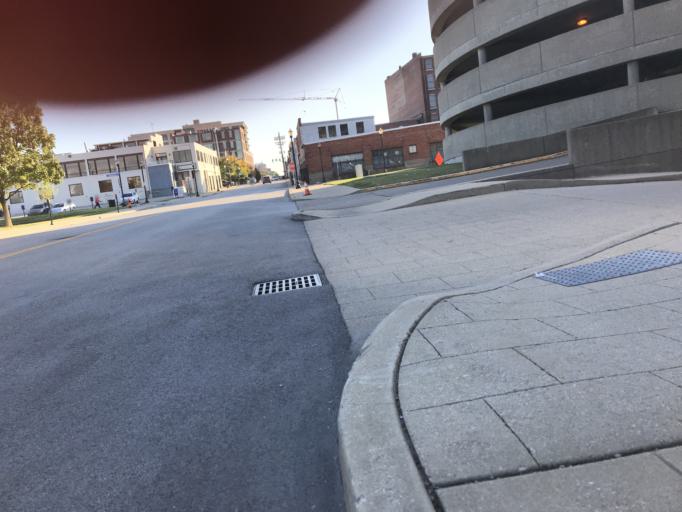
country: US
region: Kentucky
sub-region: Jefferson County
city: Louisville
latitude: 38.2572
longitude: -85.7478
